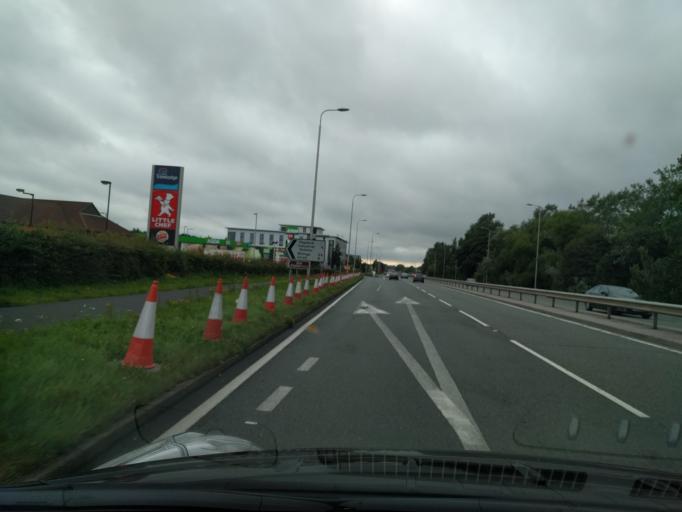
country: GB
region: England
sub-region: Borough of Wigan
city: Ashton in Makerfield
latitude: 53.4726
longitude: -2.6622
